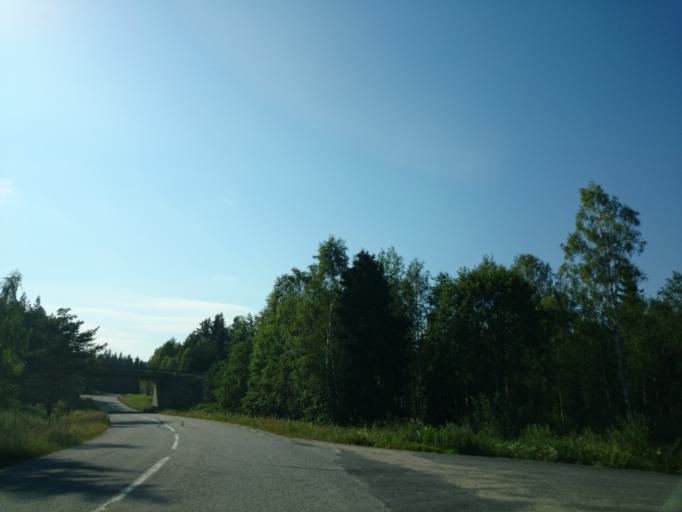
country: SE
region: Vaesternorrland
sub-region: Sundsvalls Kommun
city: Njurundabommen
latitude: 62.2133
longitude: 17.3752
